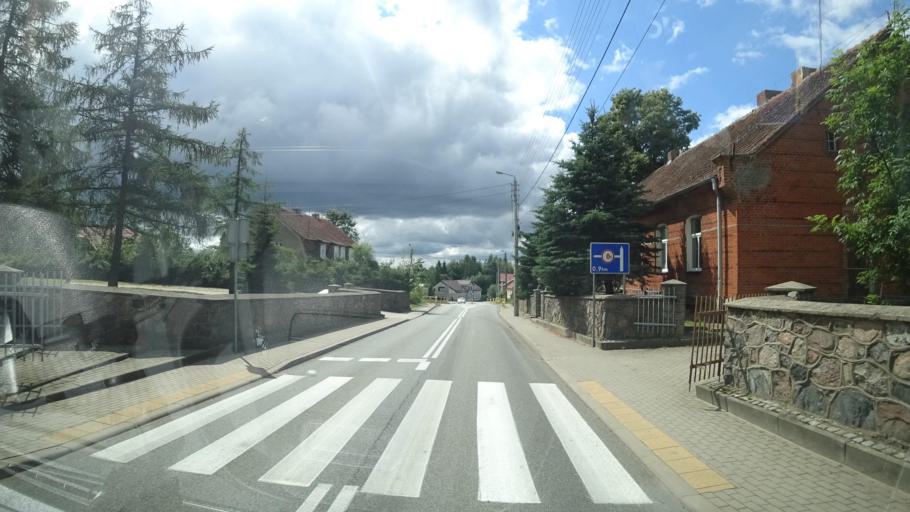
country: PL
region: Warmian-Masurian Voivodeship
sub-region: Powiat goldapski
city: Goldap
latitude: 54.2263
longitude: 22.2412
